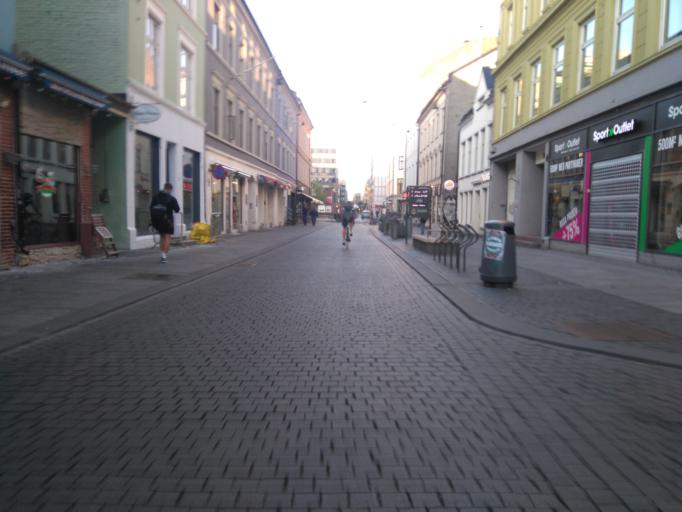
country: NO
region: Oslo
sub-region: Oslo
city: Oslo
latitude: 59.9167
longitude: 10.7528
